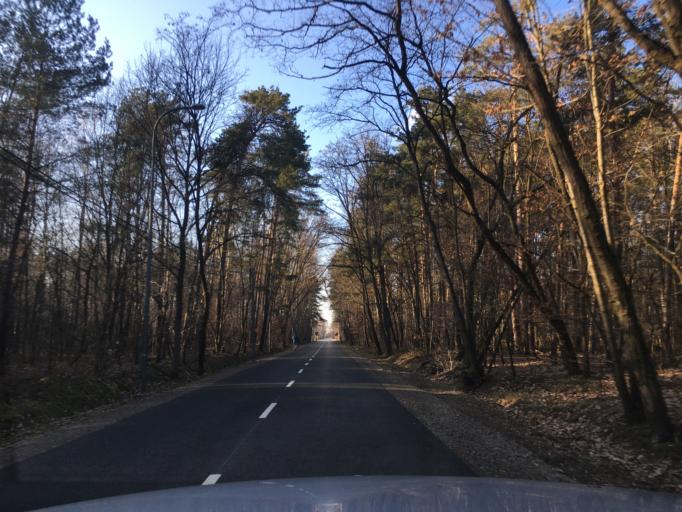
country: PL
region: Lodz Voivodeship
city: Zabia Wola
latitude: 52.0504
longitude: 20.7375
